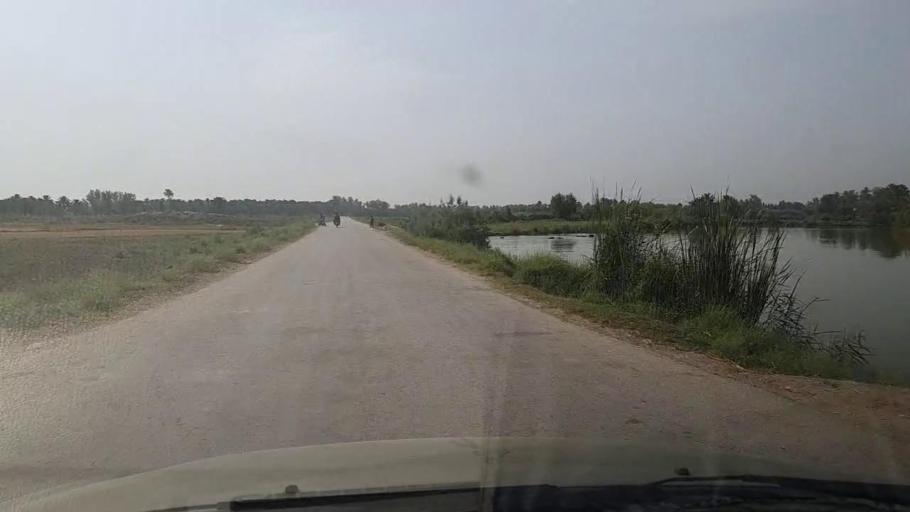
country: PK
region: Sindh
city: Gambat
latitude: 27.4590
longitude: 68.4832
